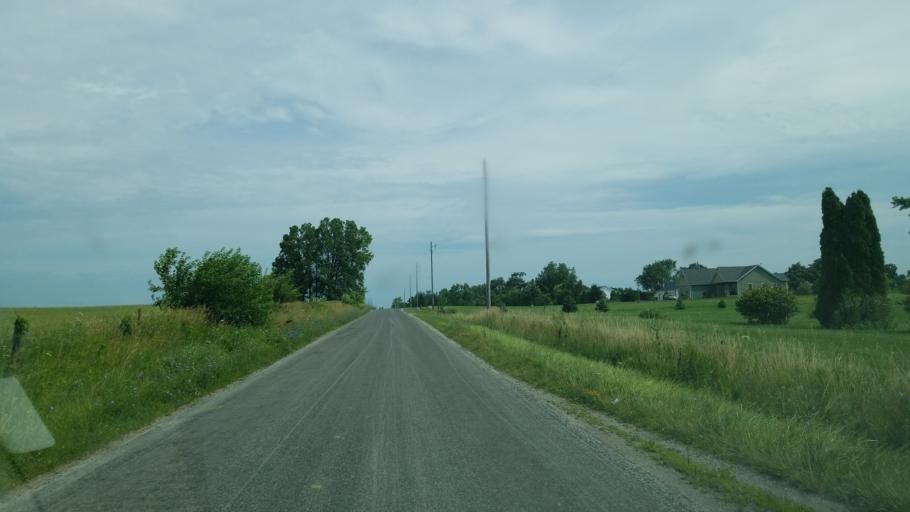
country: US
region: Ohio
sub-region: Ashland County
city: Ashland
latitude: 40.9169
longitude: -82.4070
